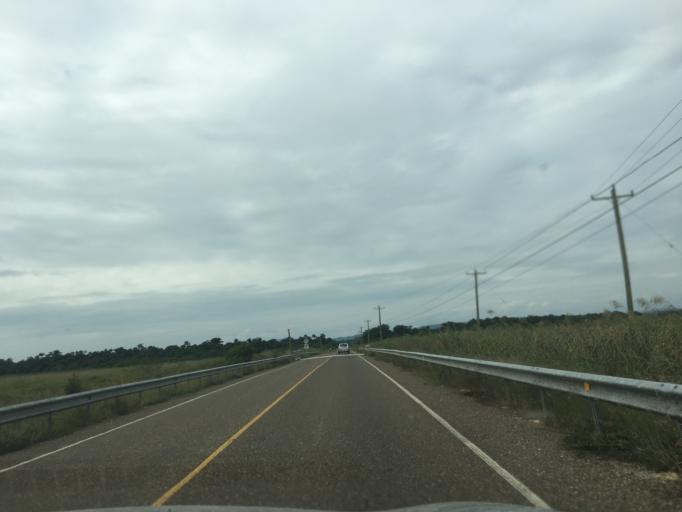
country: BZ
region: Stann Creek
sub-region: Dangriga
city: Dangriga
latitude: 16.8591
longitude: -88.2995
